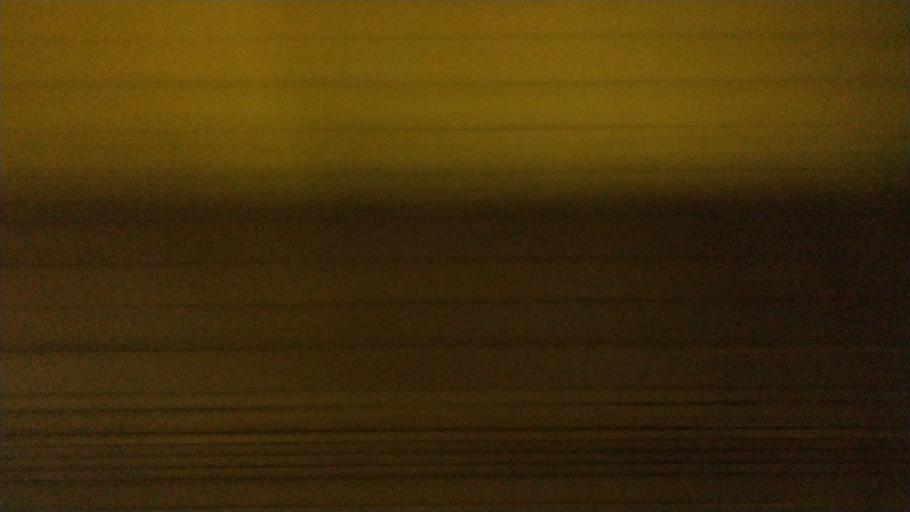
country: JP
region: Gifu
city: Nakatsugawa
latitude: 35.5913
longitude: 137.5991
